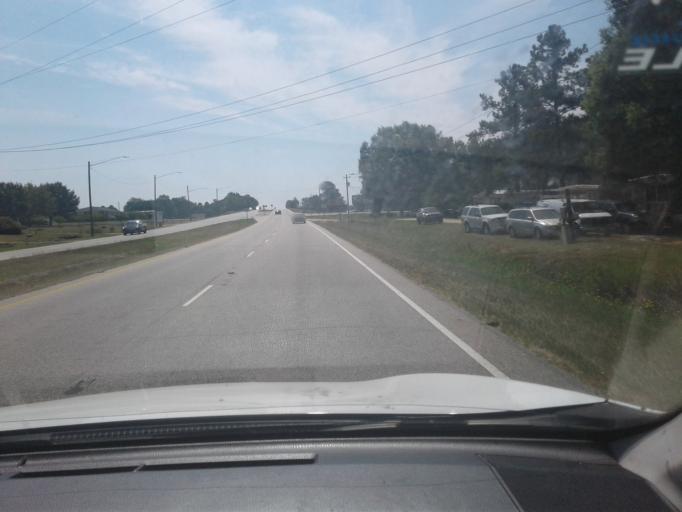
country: US
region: North Carolina
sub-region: Harnett County
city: Erwin
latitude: 35.3321
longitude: -78.6683
